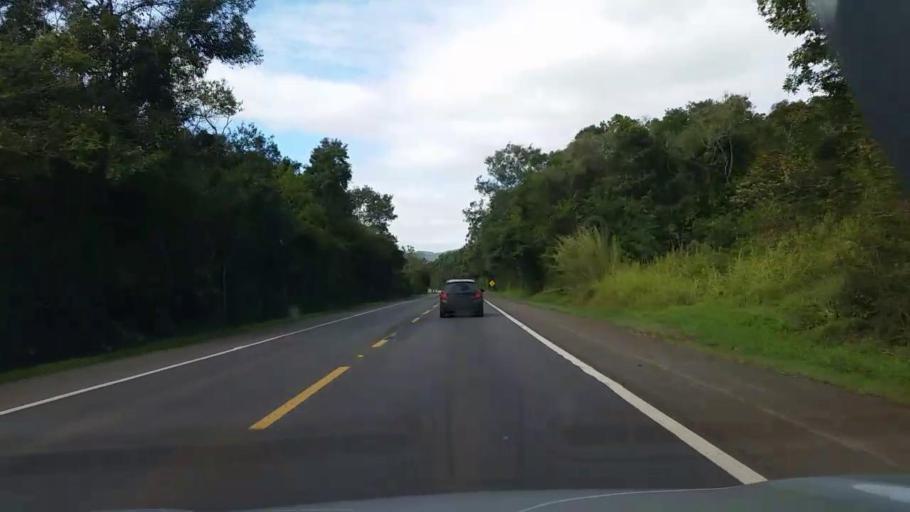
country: BR
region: Rio Grande do Sul
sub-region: Arroio Do Meio
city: Arroio do Meio
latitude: -29.3360
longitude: -52.0874
